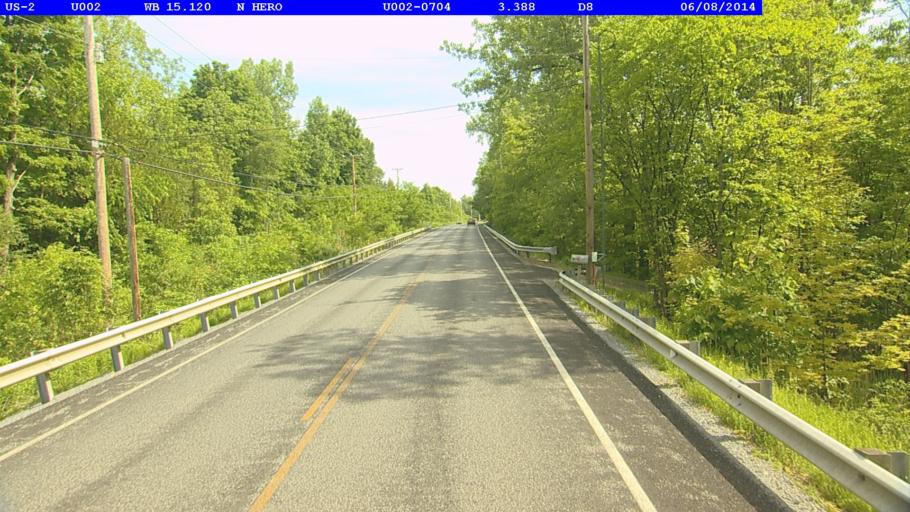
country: US
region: Vermont
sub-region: Grand Isle County
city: North Hero
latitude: 44.8433
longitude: -73.2678
